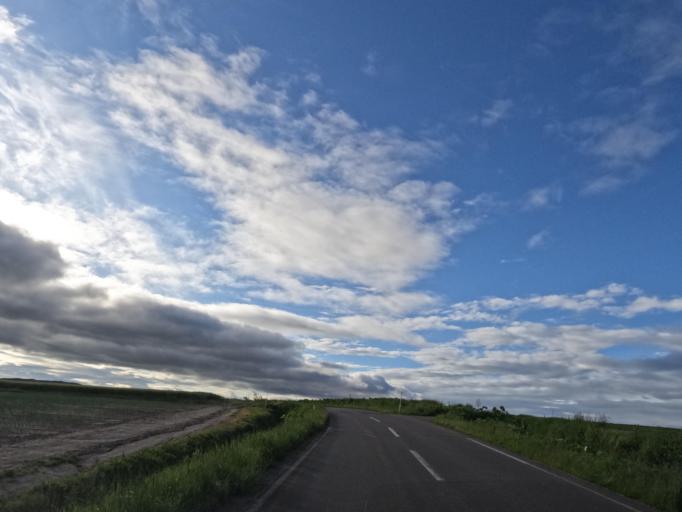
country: JP
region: Hokkaido
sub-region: Asahikawa-shi
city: Asahikawa
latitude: 43.6250
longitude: 142.4380
